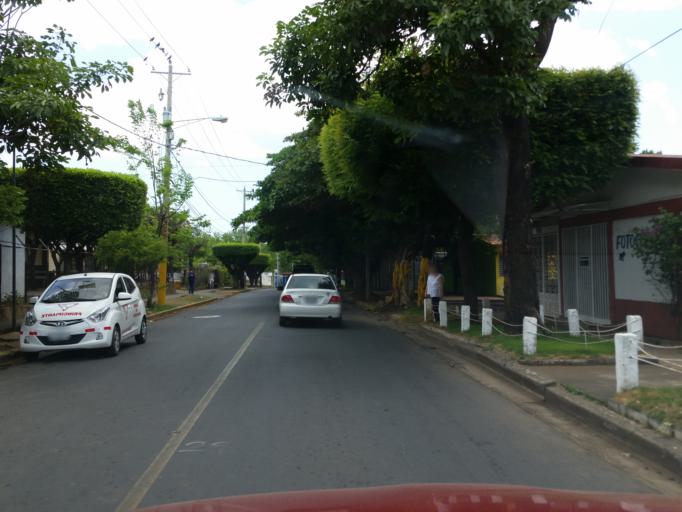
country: NI
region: Managua
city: Managua
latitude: 12.1132
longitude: -86.2485
